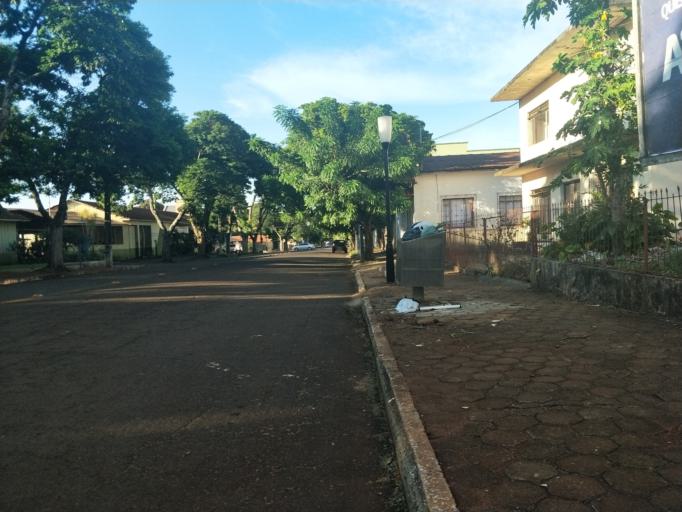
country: BR
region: Parana
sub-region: Marechal Candido Rondon
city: Marechal Candido Rondon
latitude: -24.5562
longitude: -54.0589
